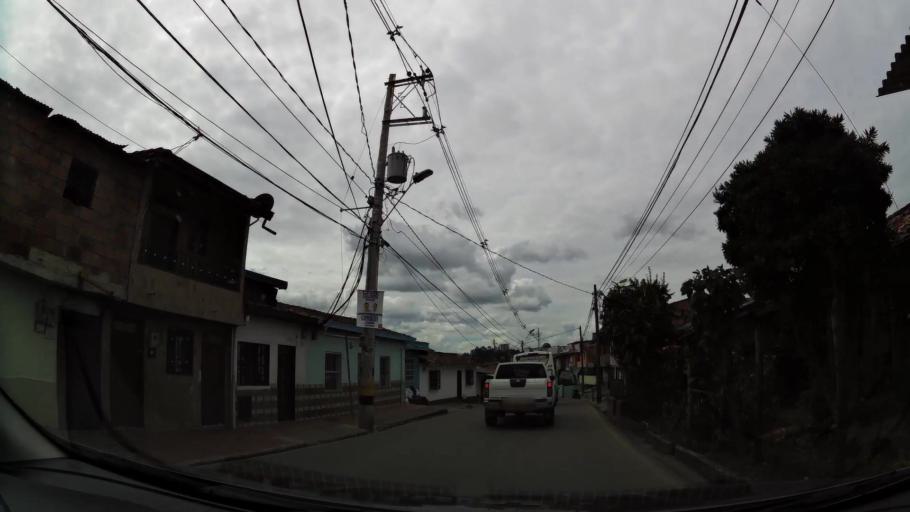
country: CO
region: Antioquia
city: Rionegro
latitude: 6.1543
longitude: -75.3651
